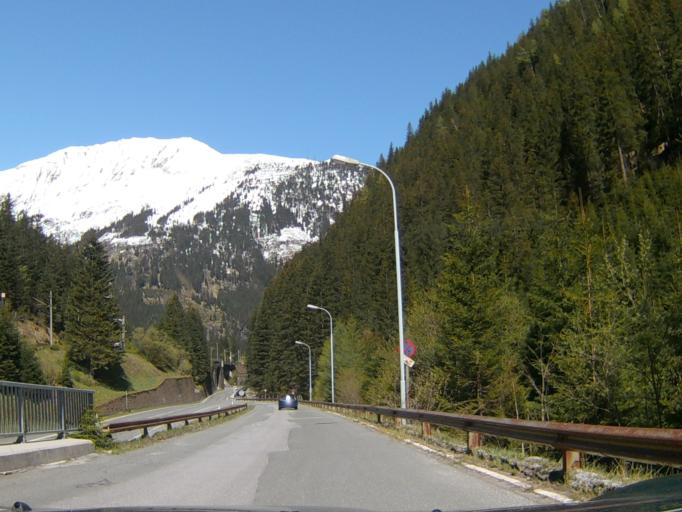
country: AT
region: Salzburg
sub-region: Politischer Bezirk Sankt Johann im Pongau
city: Bad Gastein
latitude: 47.0824
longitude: 13.1285
